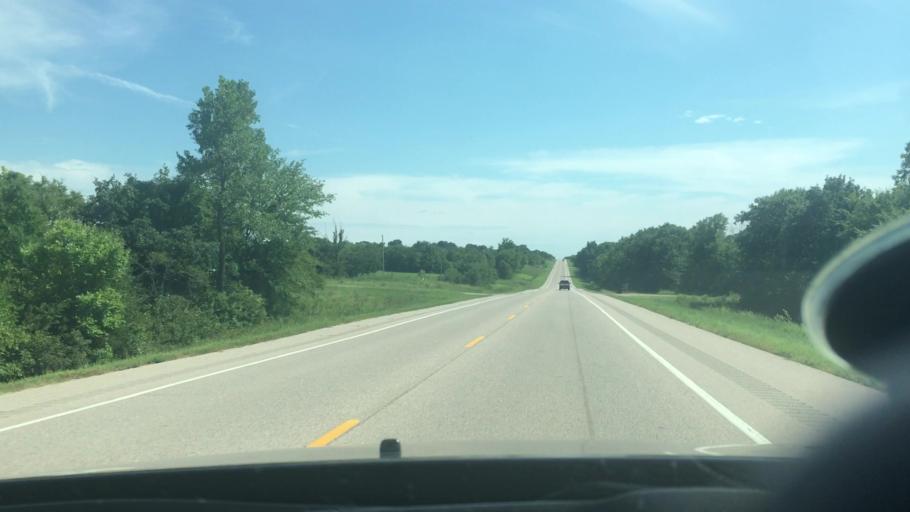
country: US
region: Oklahoma
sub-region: Seminole County
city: Konawa
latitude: 35.0112
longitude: -96.6786
